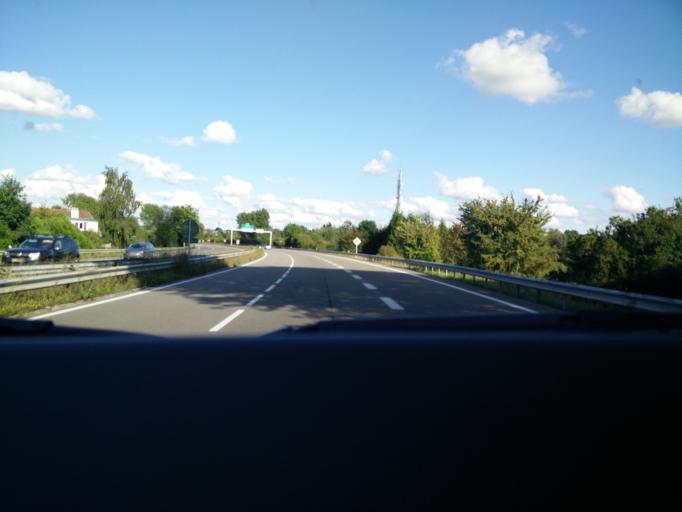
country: FR
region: Nord-Pas-de-Calais
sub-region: Departement du Nord
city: Marpent
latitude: 50.2938
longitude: 4.0683
